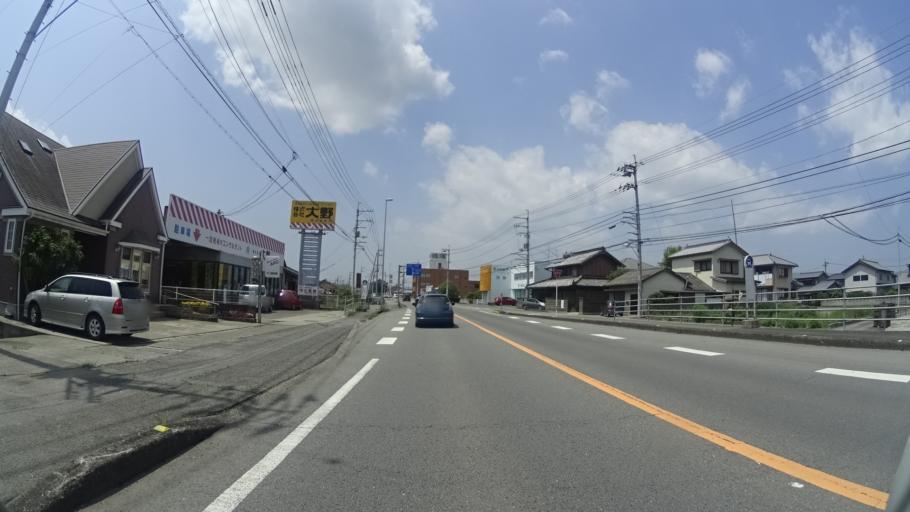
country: JP
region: Tokushima
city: Kamojimacho-jogejima
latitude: 34.0737
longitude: 134.3913
